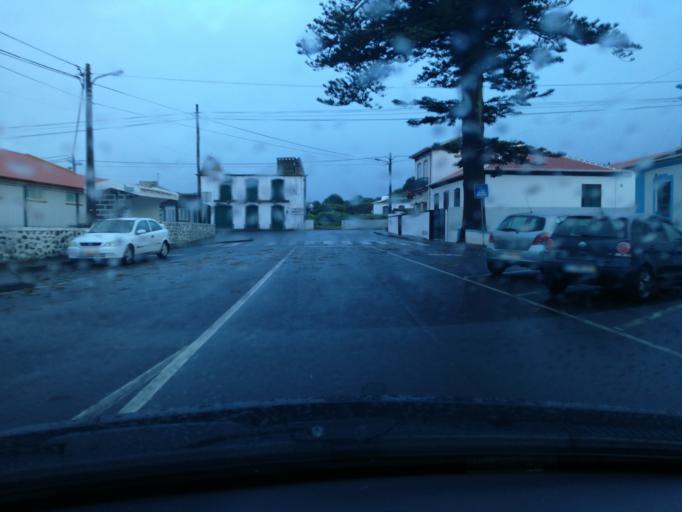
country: PT
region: Azores
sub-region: Praia da Vitoria
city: Praia da Vitoria
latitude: 38.7069
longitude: -27.0584
